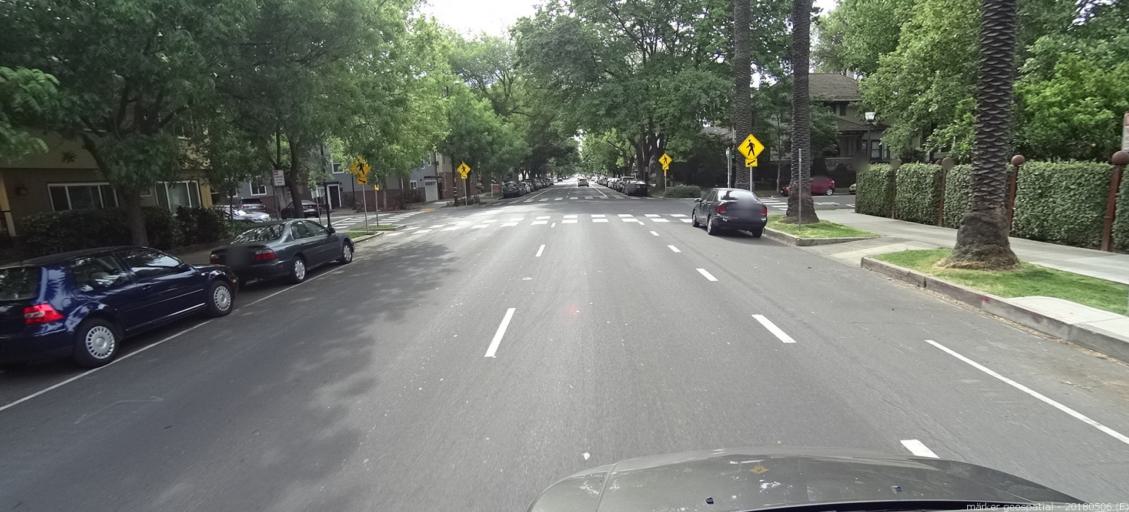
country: US
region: California
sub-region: Sacramento County
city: Sacramento
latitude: 38.5731
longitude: -121.4849
